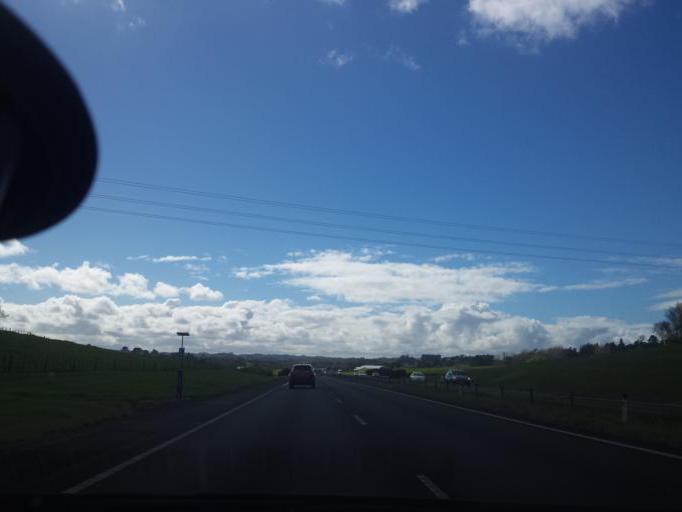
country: NZ
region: Auckland
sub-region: Auckland
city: Rothesay Bay
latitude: -36.6419
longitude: 174.6626
